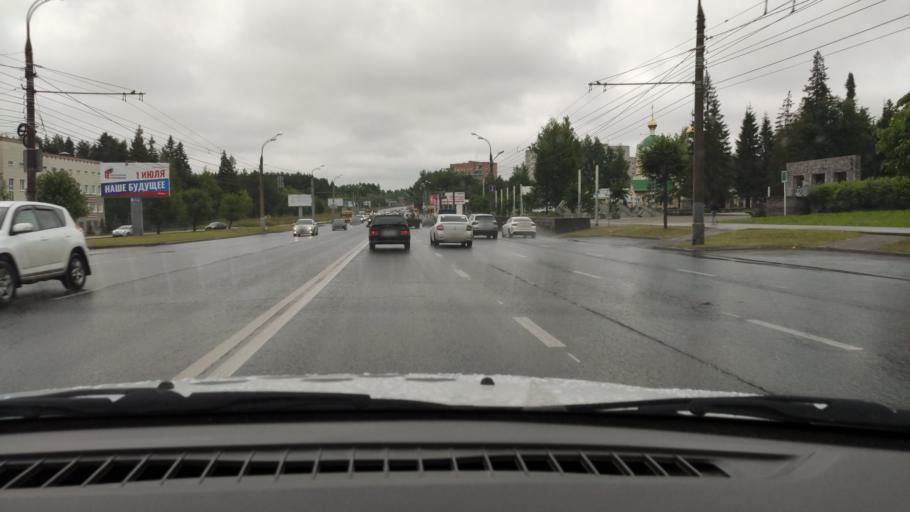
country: RU
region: Udmurtiya
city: Izhevsk
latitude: 56.8806
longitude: 53.2240
